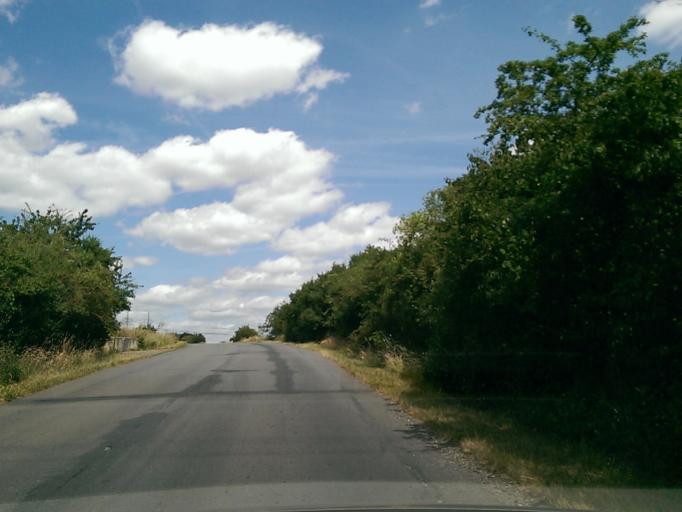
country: CZ
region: Central Bohemia
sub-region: Okres Melnik
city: Melnik
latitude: 50.3724
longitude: 14.4834
